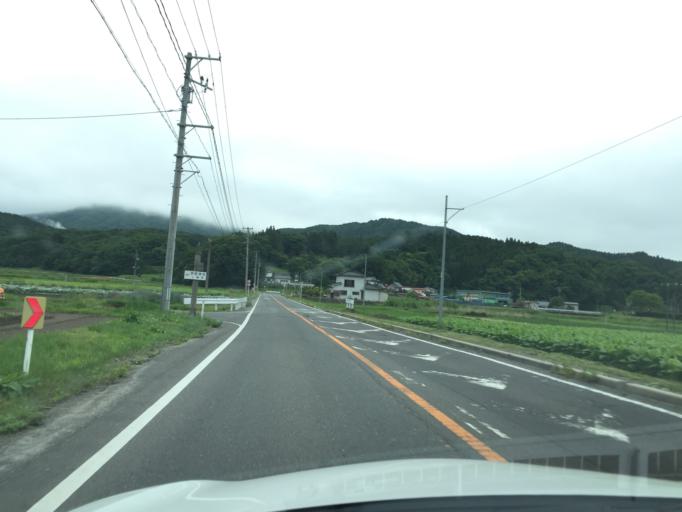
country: JP
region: Fukushima
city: Funehikimachi-funehiki
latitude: 37.2980
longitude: 140.6514
